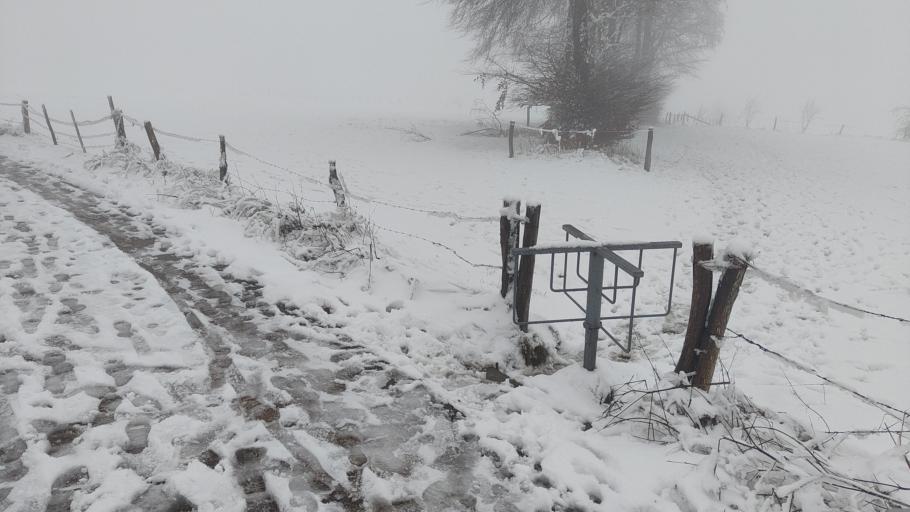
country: DE
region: North Rhine-Westphalia
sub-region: Regierungsbezirk Koln
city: Monschau
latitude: 50.5752
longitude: 6.2111
